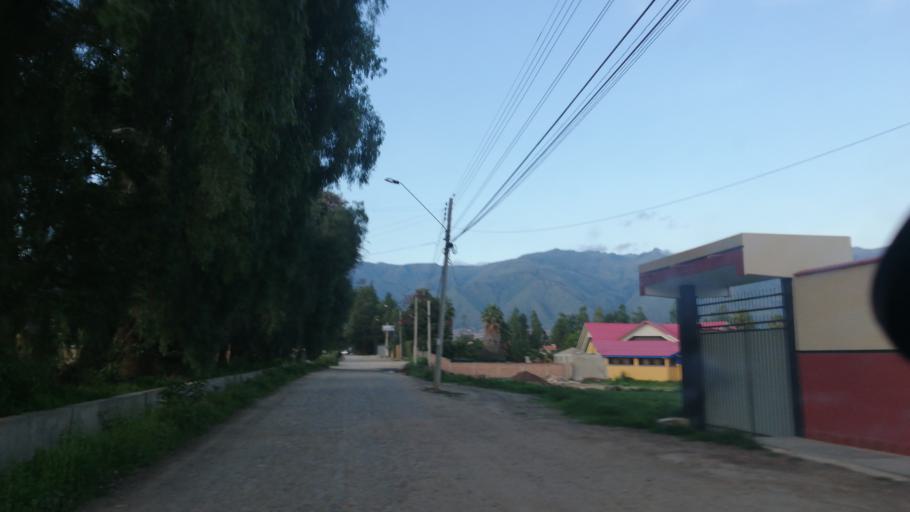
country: BO
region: Cochabamba
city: Cochabamba
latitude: -17.3796
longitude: -66.2075
